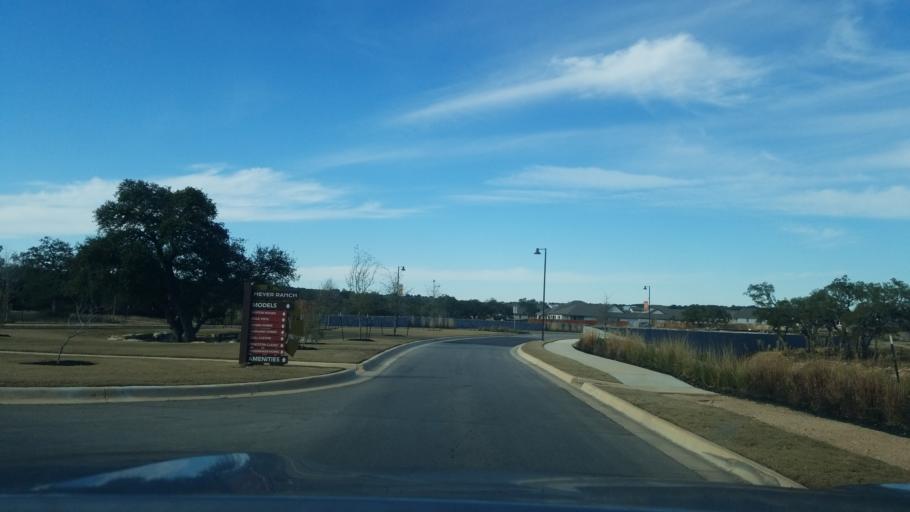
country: US
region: Texas
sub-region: Comal County
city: Canyon Lake
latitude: 29.7747
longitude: -98.2891
